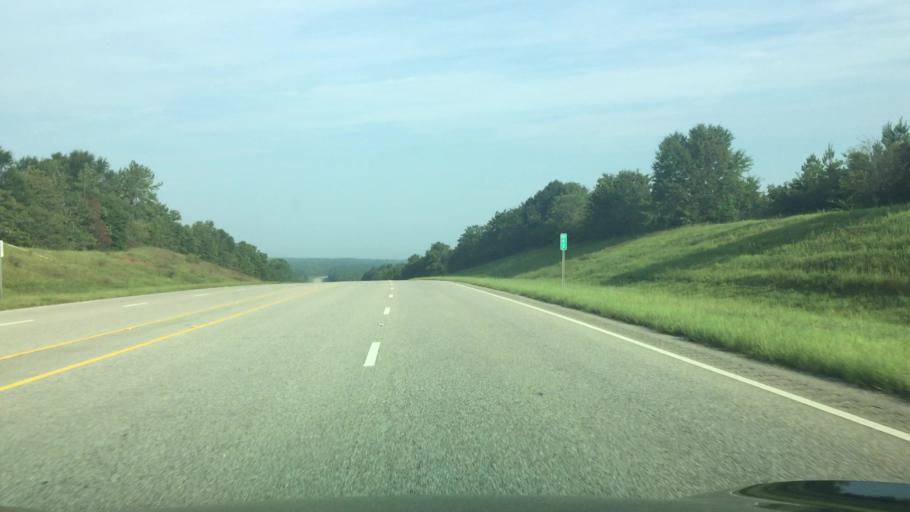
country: US
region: Alabama
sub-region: Butler County
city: Georgiana
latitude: 31.4613
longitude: -86.6442
